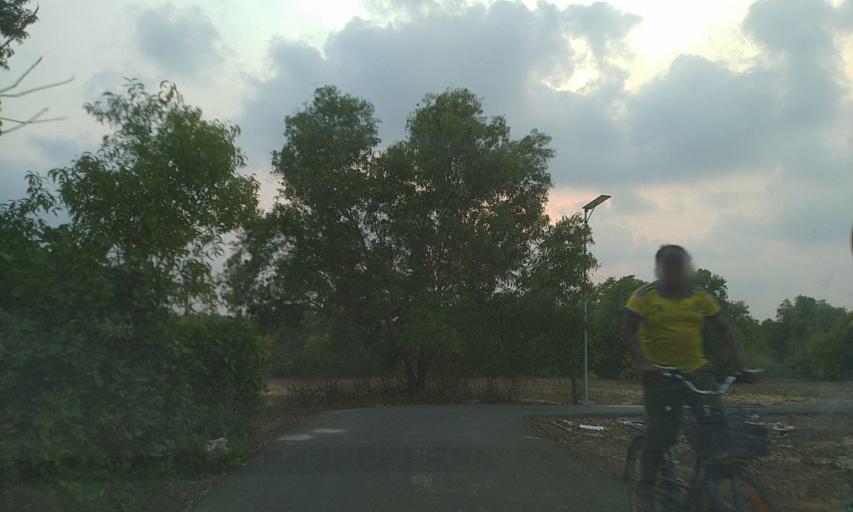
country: IN
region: Goa
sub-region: South Goa
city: Cavelossim
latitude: 15.1812
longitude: 73.9454
